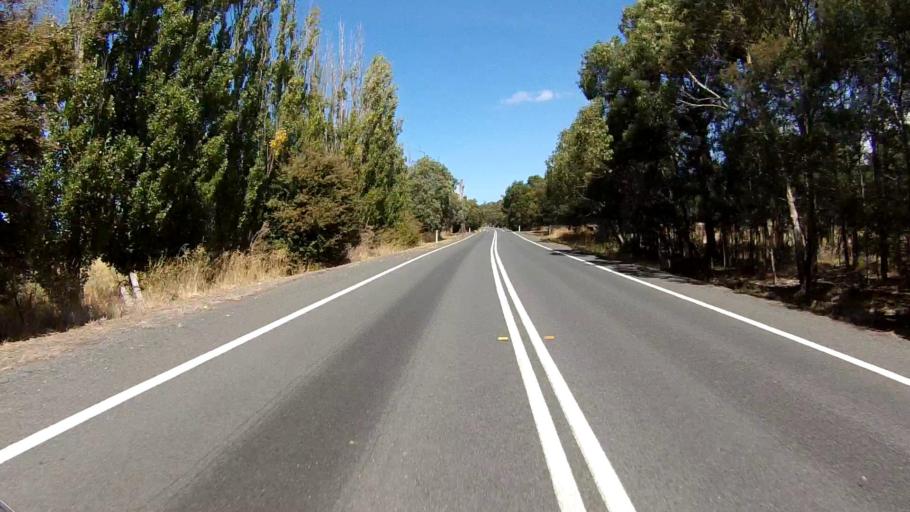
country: AU
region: Tasmania
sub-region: Break O'Day
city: St Helens
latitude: -42.0737
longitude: 148.0671
